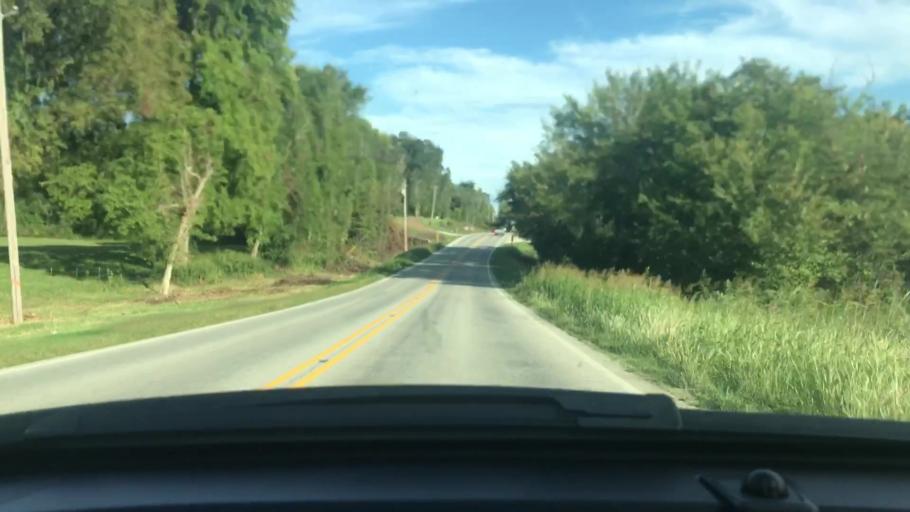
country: US
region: Arkansas
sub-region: Sharp County
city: Cherokee Village
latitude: 36.3079
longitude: -91.4562
